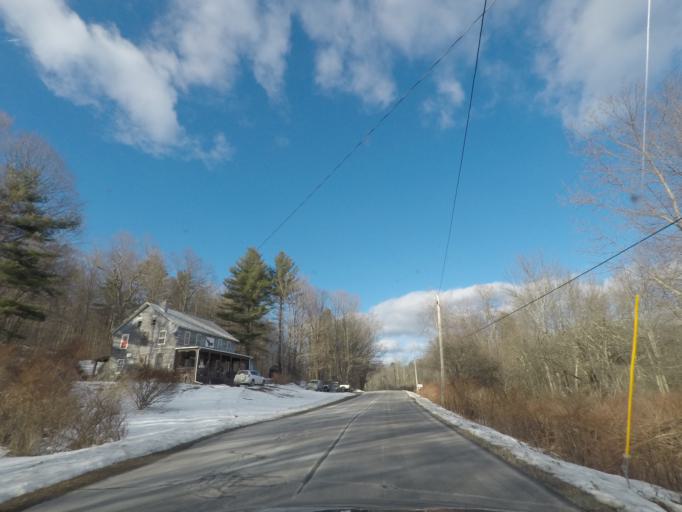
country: US
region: New York
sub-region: Rensselaer County
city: Nassau
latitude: 42.5327
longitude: -73.5291
